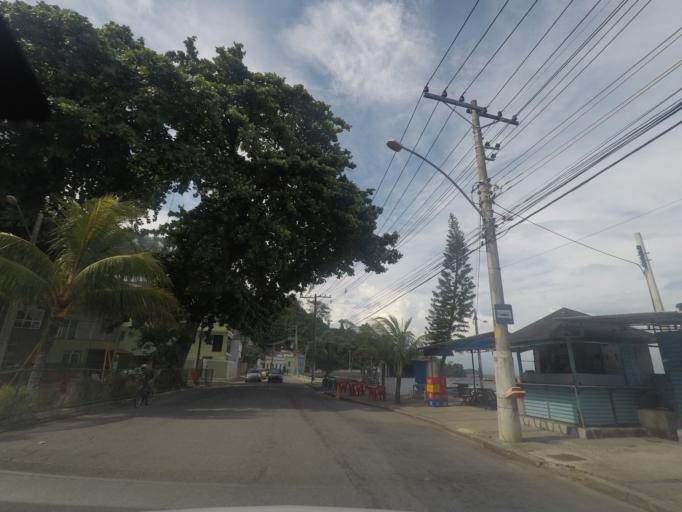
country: BR
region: Rio de Janeiro
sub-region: Rio De Janeiro
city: Rio de Janeiro
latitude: -22.8149
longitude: -43.1766
